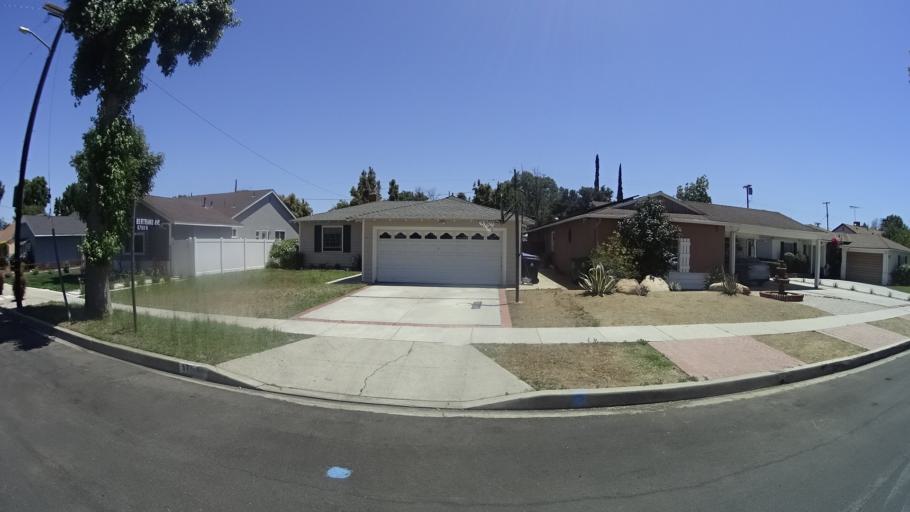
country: US
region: California
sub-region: Los Angeles County
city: Northridge
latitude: 34.1930
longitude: -118.5247
